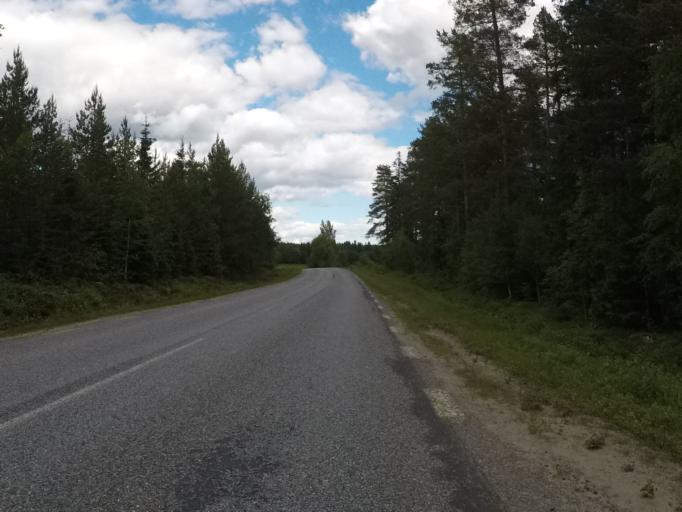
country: SE
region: Vaesterbotten
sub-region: Umea Kommun
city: Saevar
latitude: 63.9388
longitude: 20.7858
